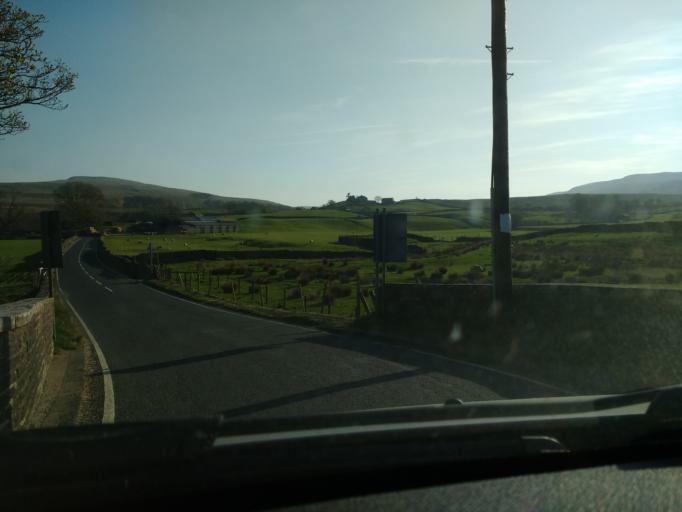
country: GB
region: England
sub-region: Cumbria
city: Kirkby Stephen
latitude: 54.3140
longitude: -2.2200
